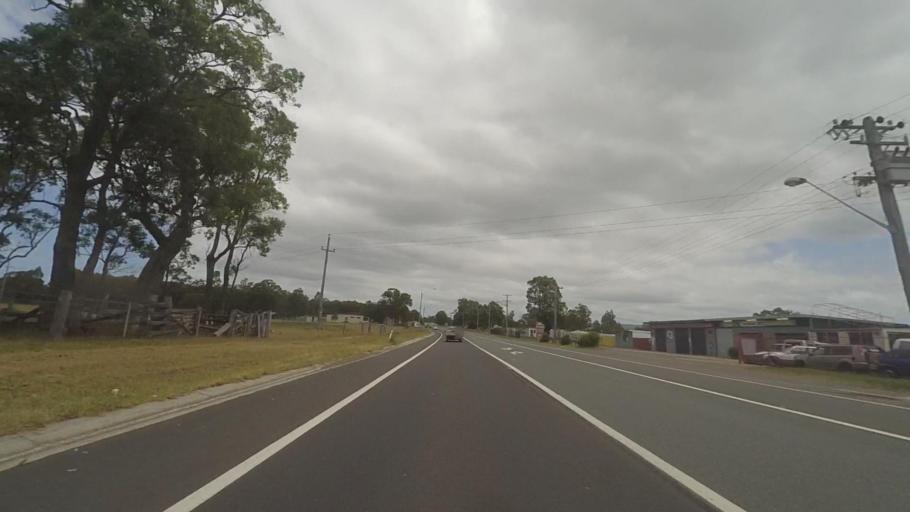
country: AU
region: New South Wales
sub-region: Shoalhaven Shire
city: Falls Creek
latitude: -35.0875
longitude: 150.5127
